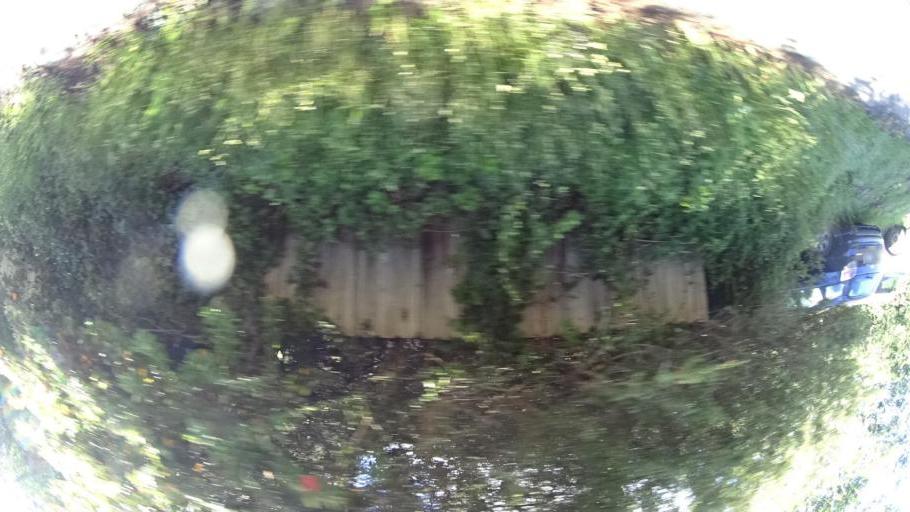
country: US
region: California
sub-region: Humboldt County
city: Westhaven-Moonstone
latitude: 41.0358
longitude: -124.1136
